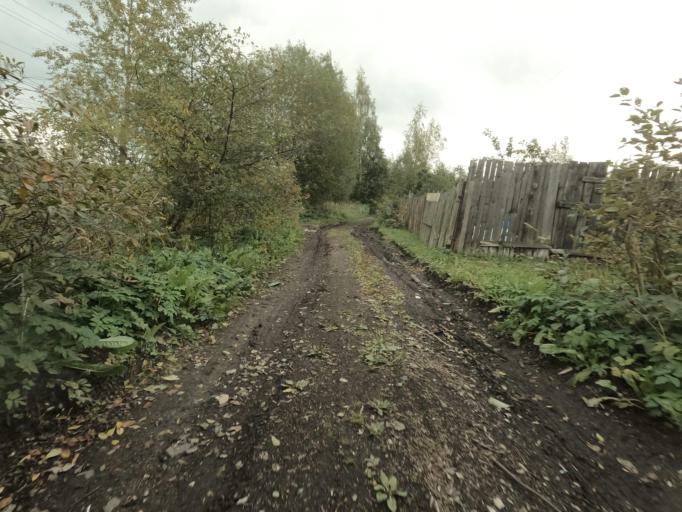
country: RU
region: St.-Petersburg
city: Sapernyy
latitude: 59.7787
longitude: 30.6381
